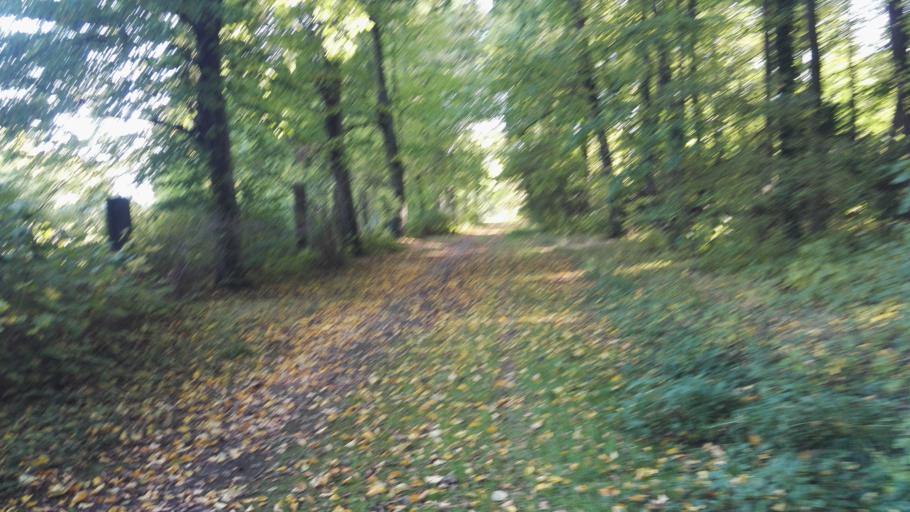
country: DE
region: Saxony
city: Dresden
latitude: 51.0402
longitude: 13.7591
